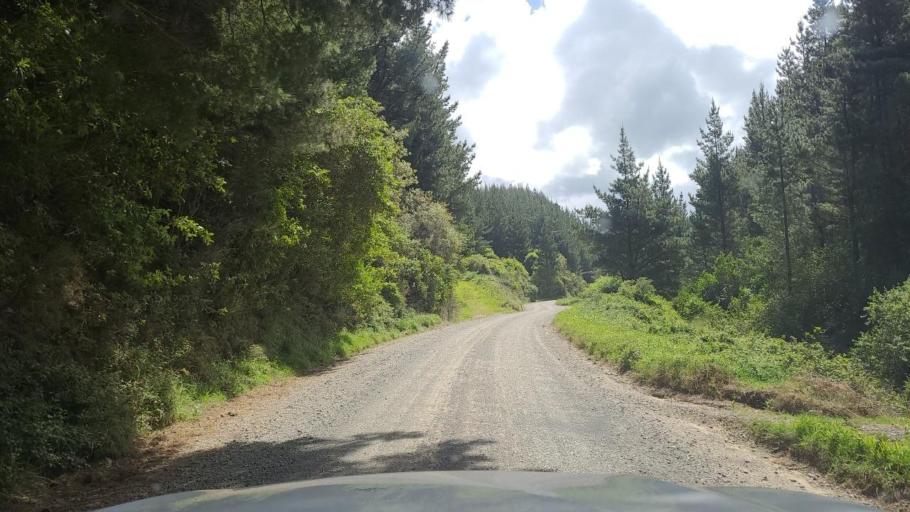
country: NZ
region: Hawke's Bay
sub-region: Napier City
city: Taradale
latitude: -39.2743
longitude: 176.6632
